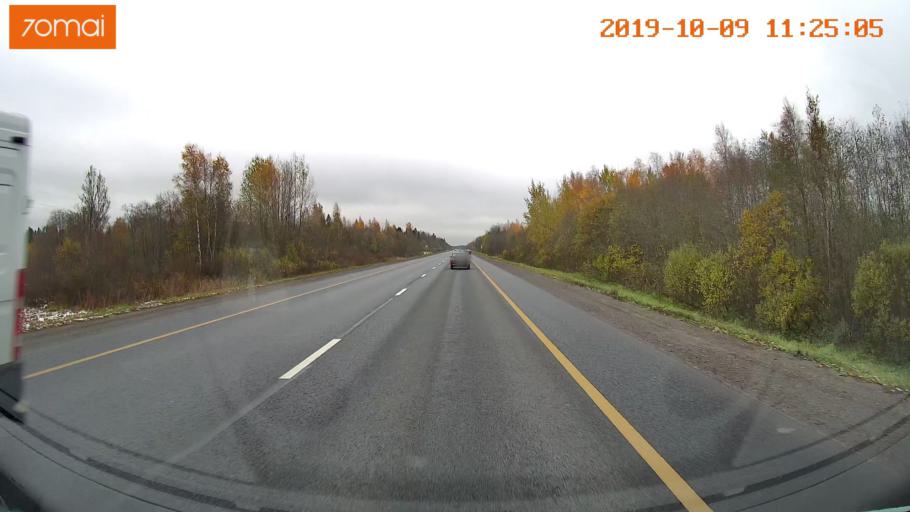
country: RU
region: Vologda
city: Vologda
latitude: 59.1049
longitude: 39.9873
